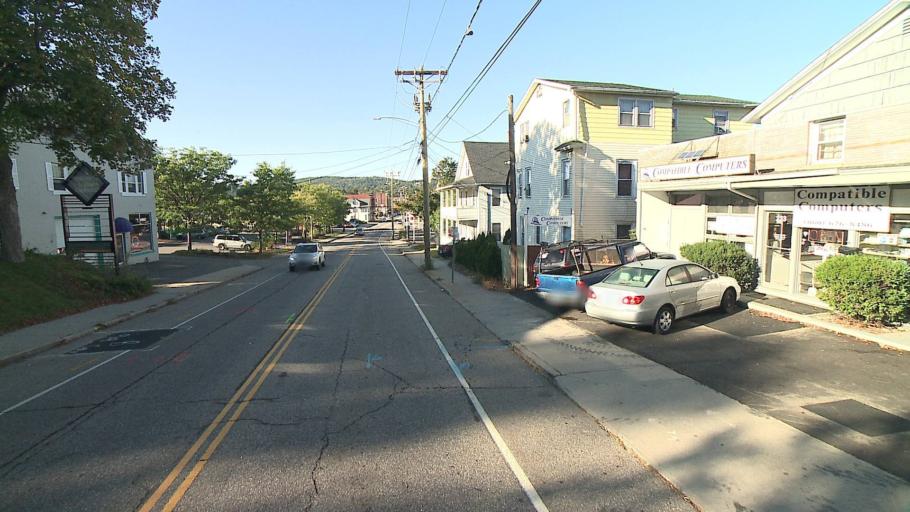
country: US
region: Connecticut
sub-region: Litchfield County
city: Torrington
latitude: 41.8039
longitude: -73.1165
